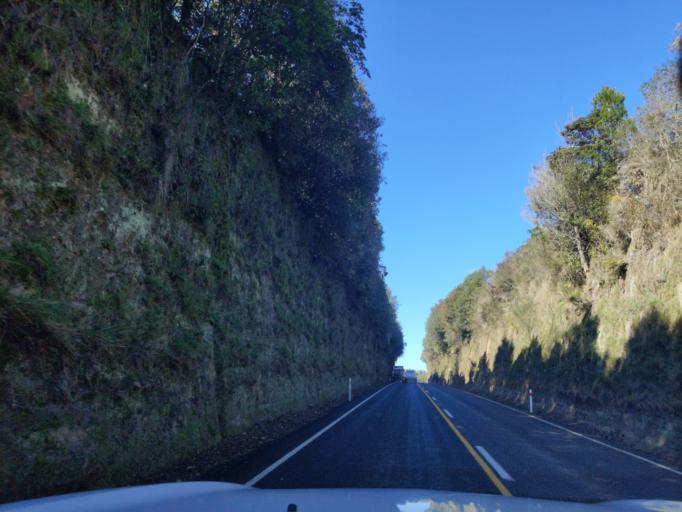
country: NZ
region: Waikato
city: Turangi
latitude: -38.7770
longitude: 175.6723
